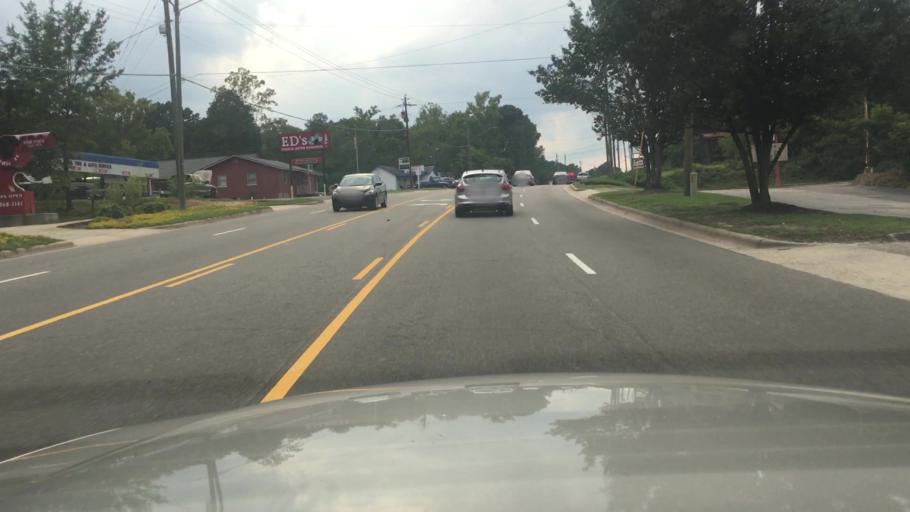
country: US
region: North Carolina
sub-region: Cumberland County
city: Fort Bragg
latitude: 35.0835
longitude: -78.9701
